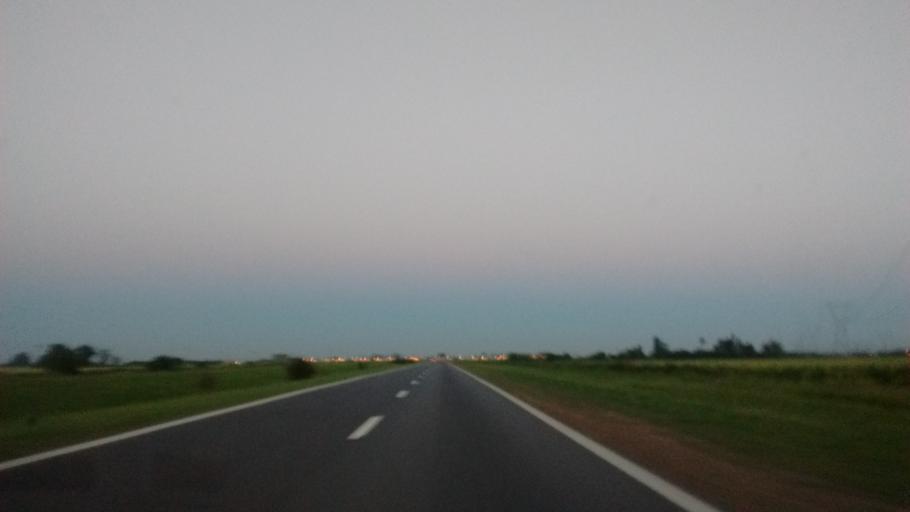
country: AR
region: Santa Fe
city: Roldan
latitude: -32.9231
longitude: -60.9161
